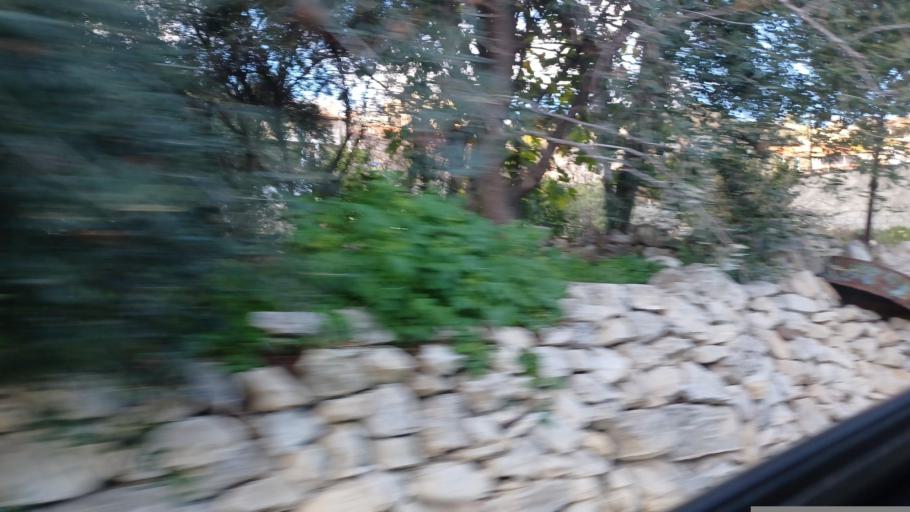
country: CY
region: Limassol
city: Pachna
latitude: 34.8318
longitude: 32.7905
